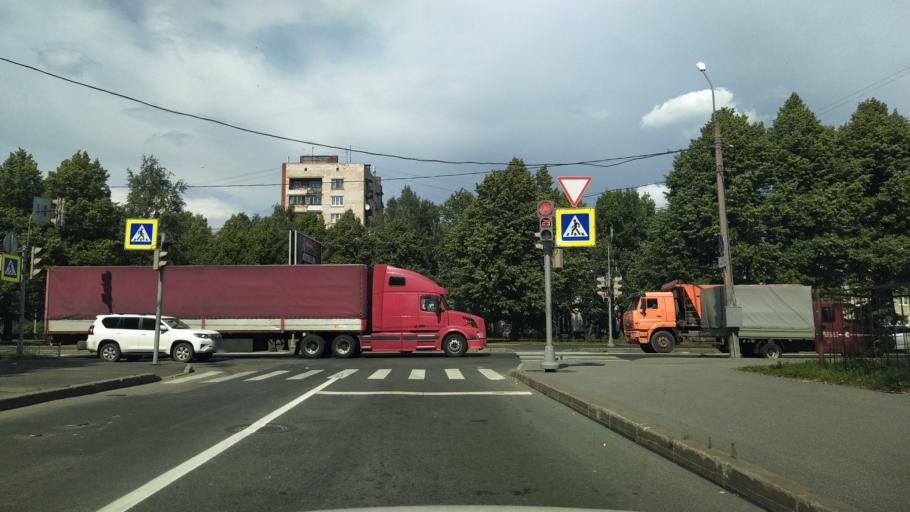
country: RU
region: Leningrad
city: Kalininskiy
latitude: 59.9651
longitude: 30.3998
